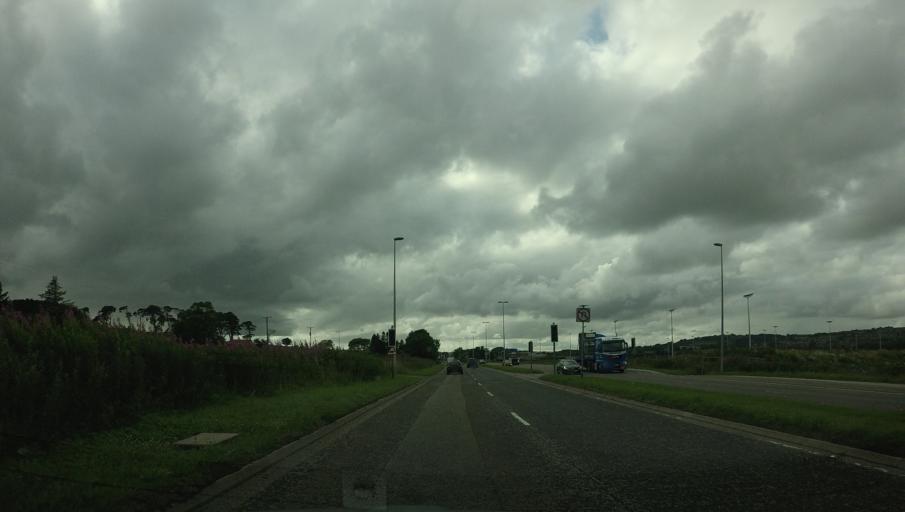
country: GB
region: Scotland
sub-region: Aberdeenshire
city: Westhill
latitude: 57.1471
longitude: -2.2537
